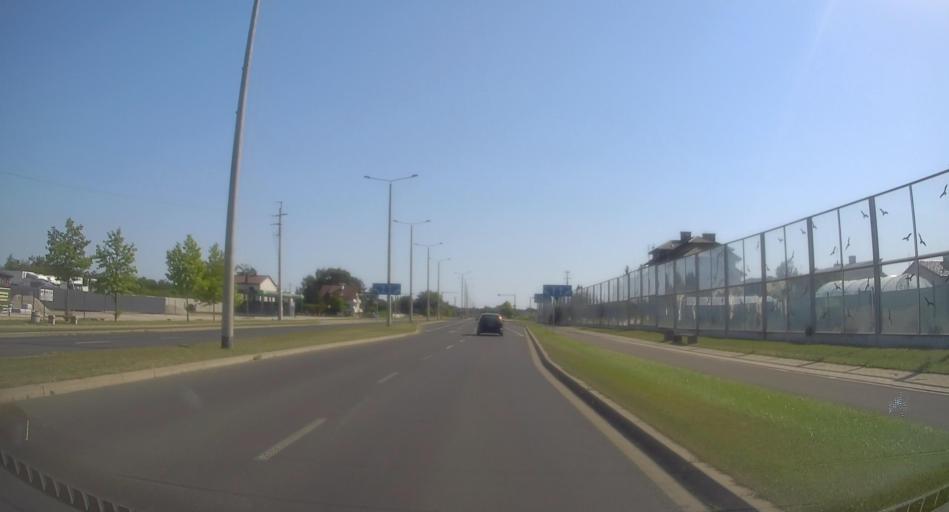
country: PL
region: Lodz Voivodeship
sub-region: Skierniewice
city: Skierniewice
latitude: 51.9493
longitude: 20.1590
